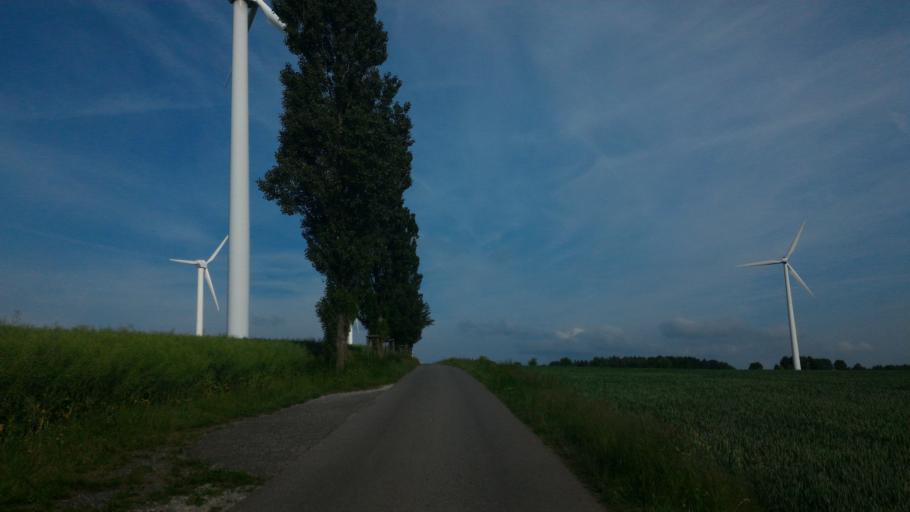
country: DE
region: Saxony
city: Leutersdorf
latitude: 50.9612
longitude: 14.6323
